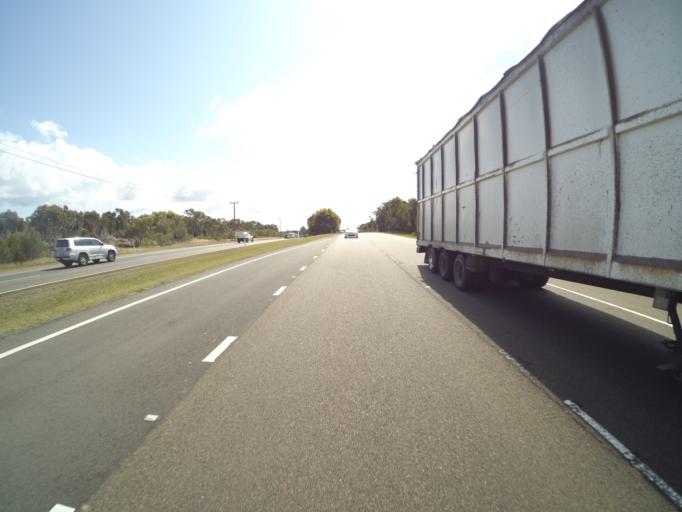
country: AU
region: New South Wales
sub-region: Sutherland Shire
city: Heathcote
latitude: -34.1126
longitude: 150.9926
